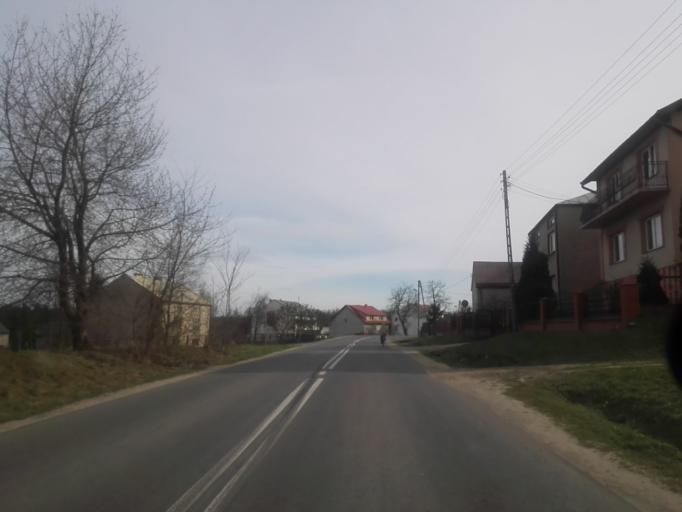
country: PL
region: Silesian Voivodeship
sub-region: Powiat czestochowski
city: Olsztyn
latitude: 50.7289
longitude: 19.3326
